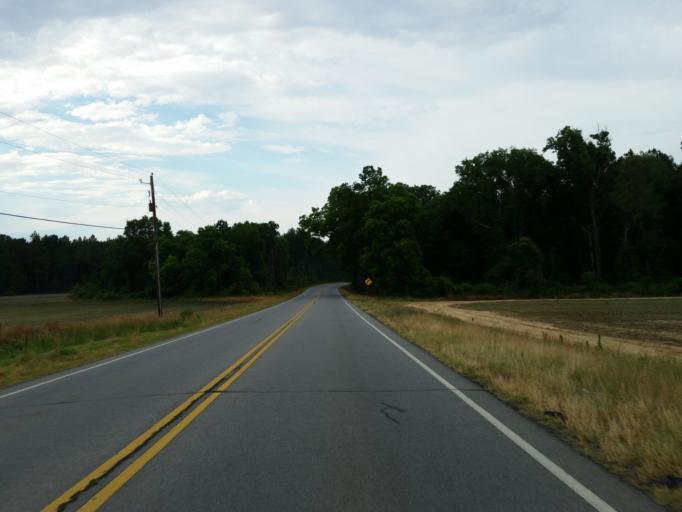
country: US
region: Georgia
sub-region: Dooly County
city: Vienna
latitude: 32.0642
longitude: -83.7983
